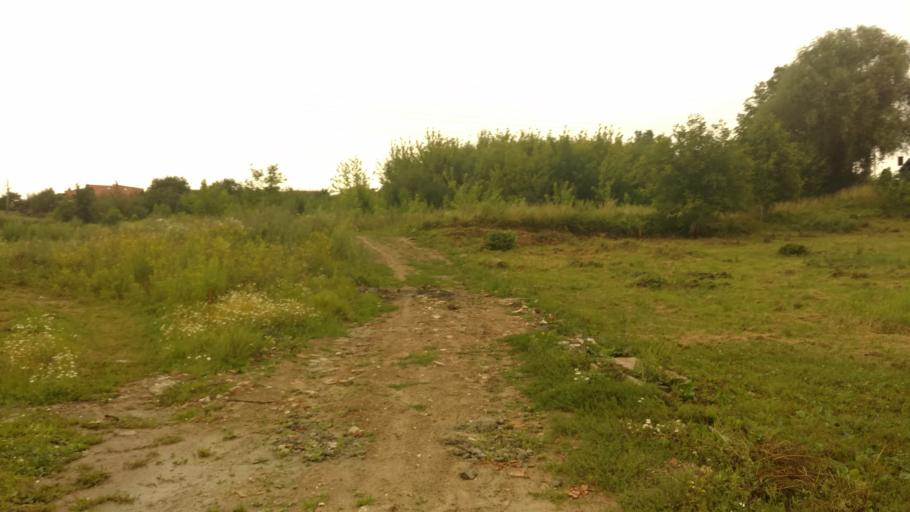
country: PL
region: Lesser Poland Voivodeship
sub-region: Powiat krakowski
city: Michalowice
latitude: 50.1387
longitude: 19.9685
